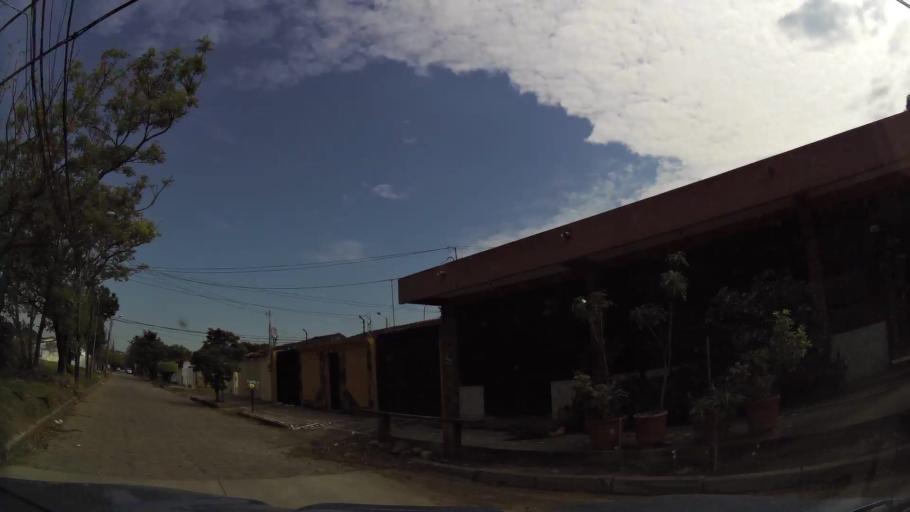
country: BO
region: Santa Cruz
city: Santa Cruz de la Sierra
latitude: -17.7506
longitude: -63.1558
